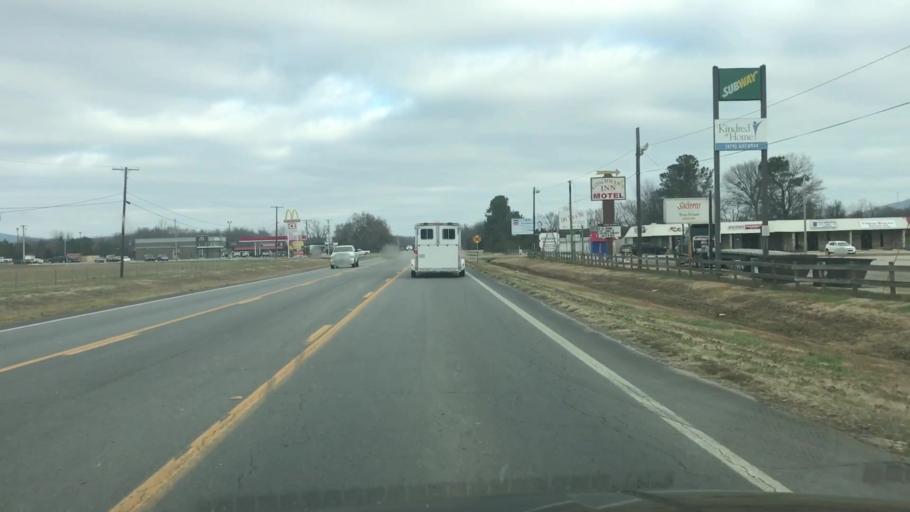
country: US
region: Arkansas
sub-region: Scott County
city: Waldron
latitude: 34.9021
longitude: -94.1074
